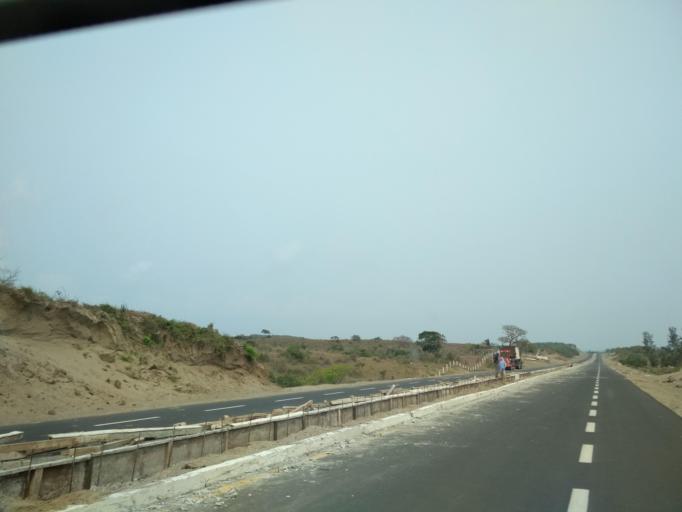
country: MX
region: Veracruz
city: Anton Lizardo
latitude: 19.0441
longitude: -95.9953
